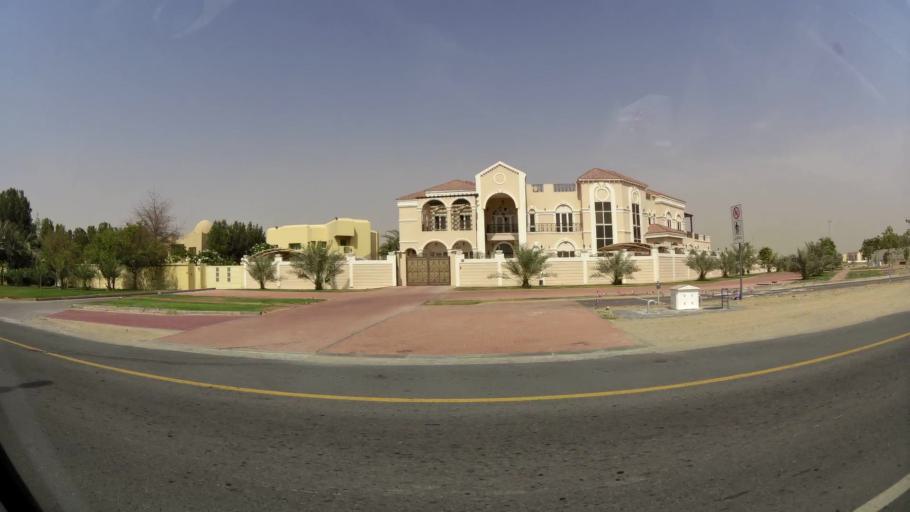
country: AE
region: Ash Shariqah
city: Sharjah
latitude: 25.2521
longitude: 55.4695
